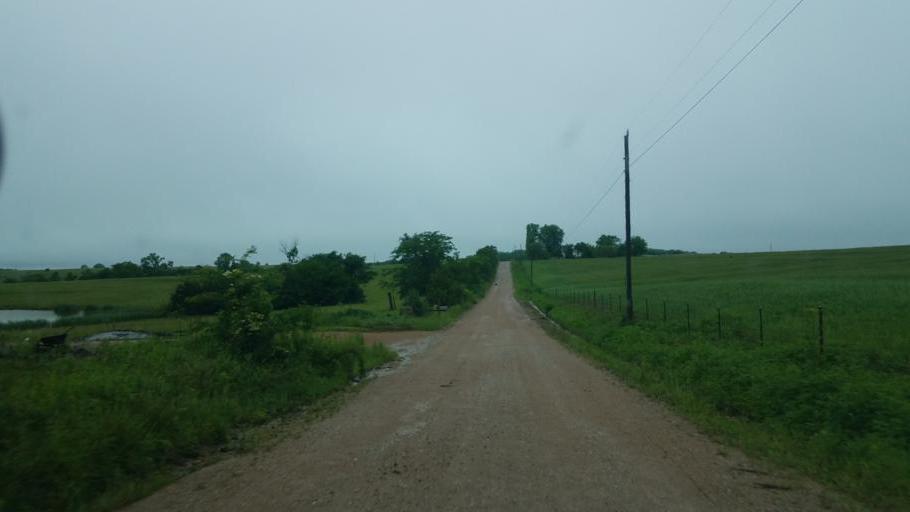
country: US
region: Missouri
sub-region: Moniteau County
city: California
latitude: 38.7493
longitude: -92.6057
